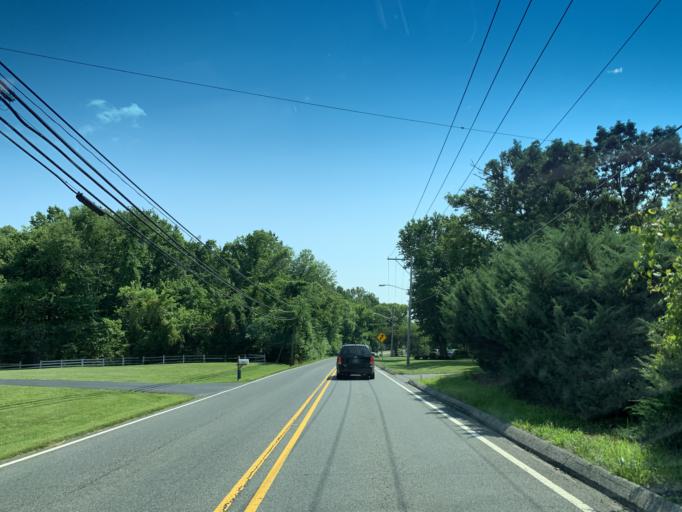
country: US
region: Maryland
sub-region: Montgomery County
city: Poolesville
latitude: 39.1769
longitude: -77.4137
